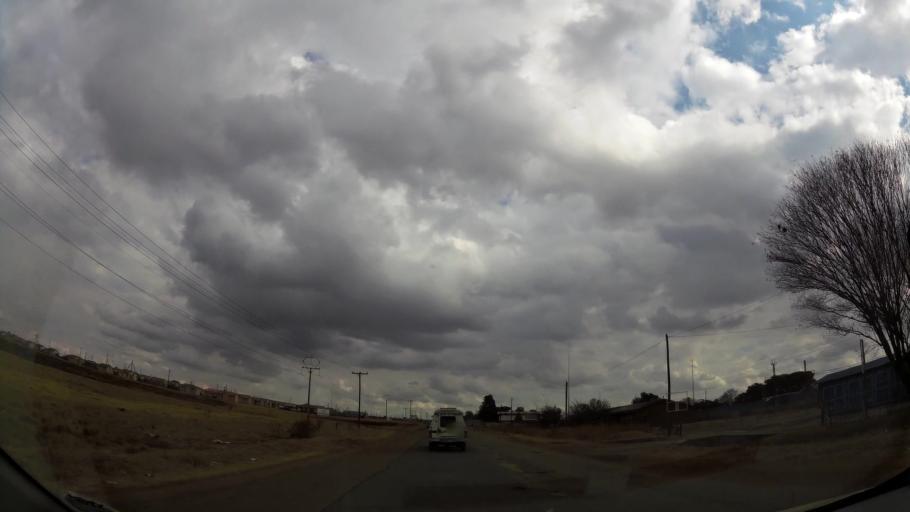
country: ZA
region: Orange Free State
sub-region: Fezile Dabi District Municipality
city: Sasolburg
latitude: -26.8555
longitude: 27.8665
